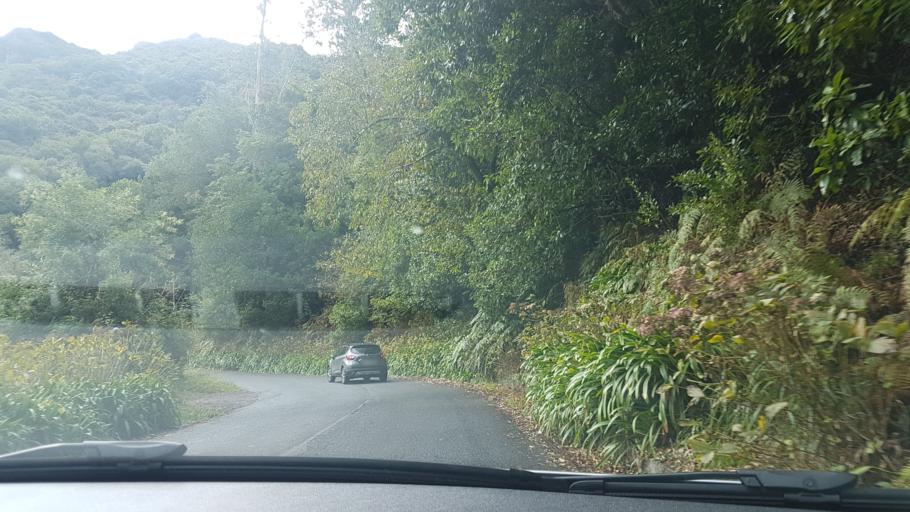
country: PT
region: Madeira
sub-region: Sao Vicente
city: Sao Vicente
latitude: 32.7640
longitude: -17.0219
